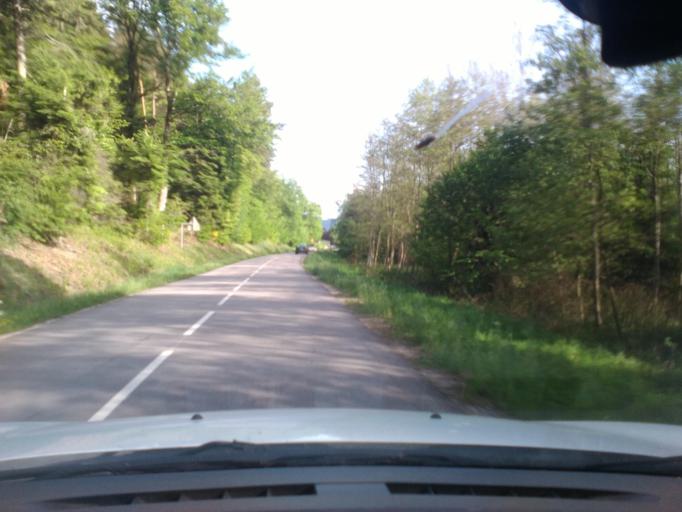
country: FR
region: Lorraine
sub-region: Departement des Vosges
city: Bruyeres
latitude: 48.2507
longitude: 6.7297
